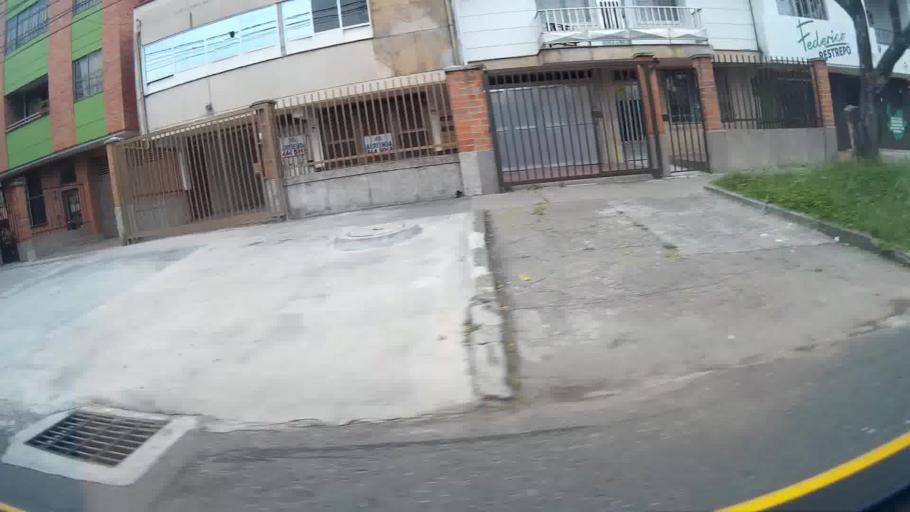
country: CO
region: Antioquia
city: Medellin
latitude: 6.2340
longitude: -75.5873
